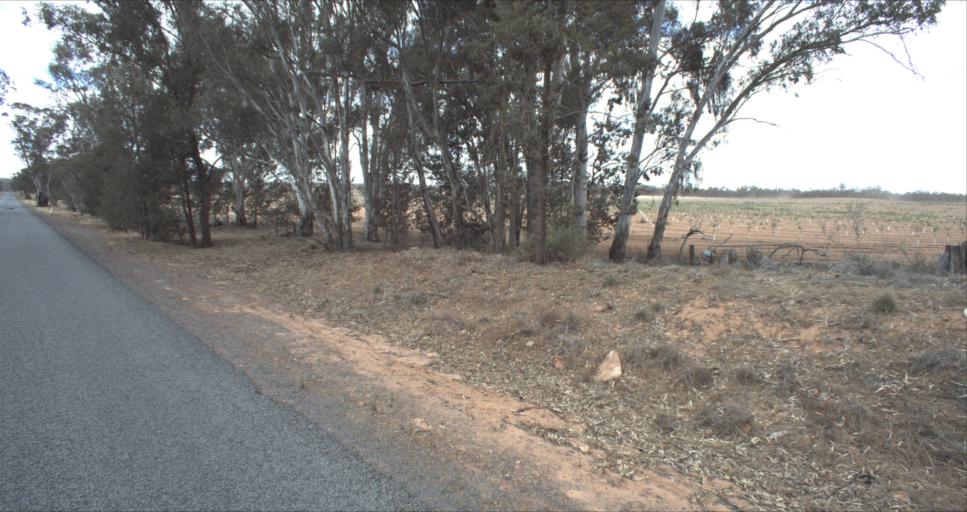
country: AU
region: New South Wales
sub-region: Leeton
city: Leeton
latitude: -34.6554
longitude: 146.3504
